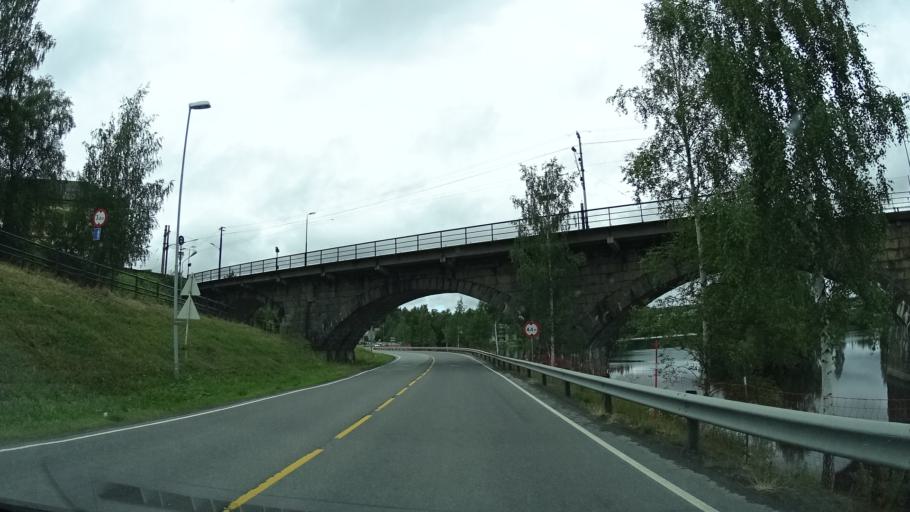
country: NO
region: Buskerud
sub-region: Ringerike
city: Honefoss
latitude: 60.1694
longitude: 10.2509
